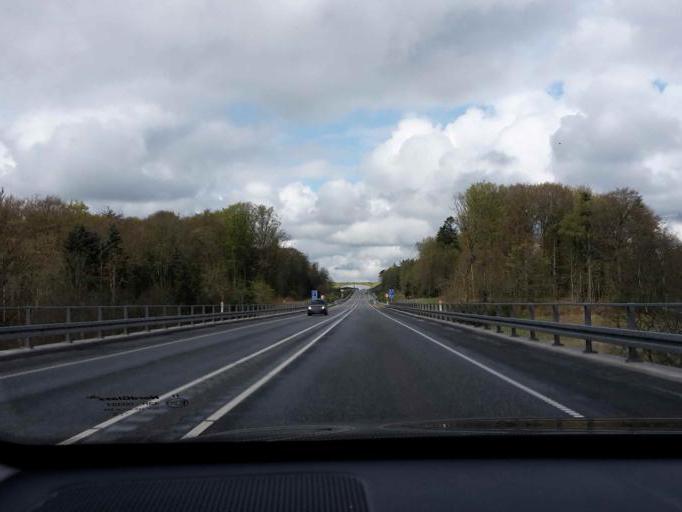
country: DK
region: South Denmark
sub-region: Vejle Kommune
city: Egtved
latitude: 55.7056
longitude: 9.2774
